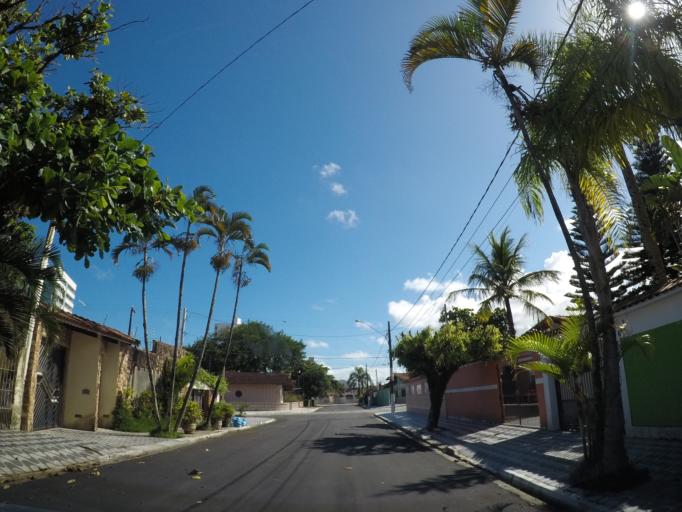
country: BR
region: Sao Paulo
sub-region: Mongagua
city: Mongagua
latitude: -24.0666
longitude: -46.5619
